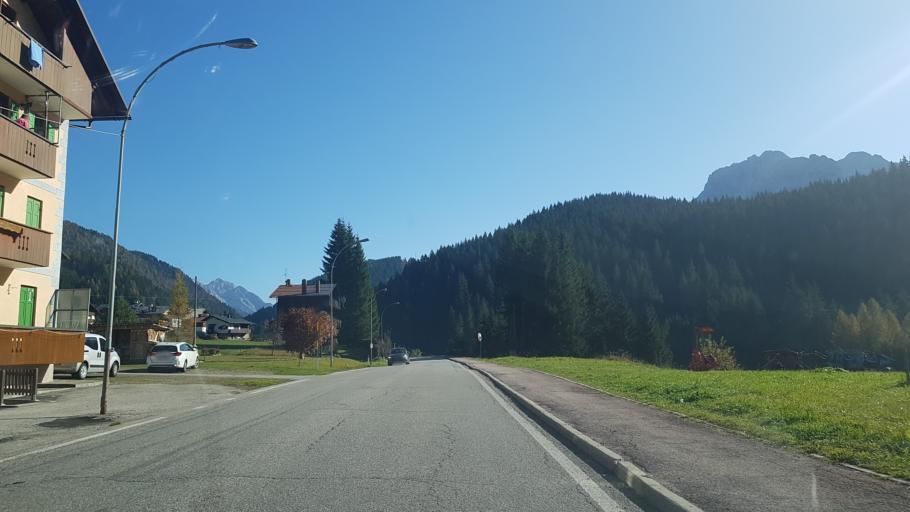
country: IT
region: Veneto
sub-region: Provincia di Belluno
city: Granvilla
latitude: 46.5687
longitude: 12.7029
